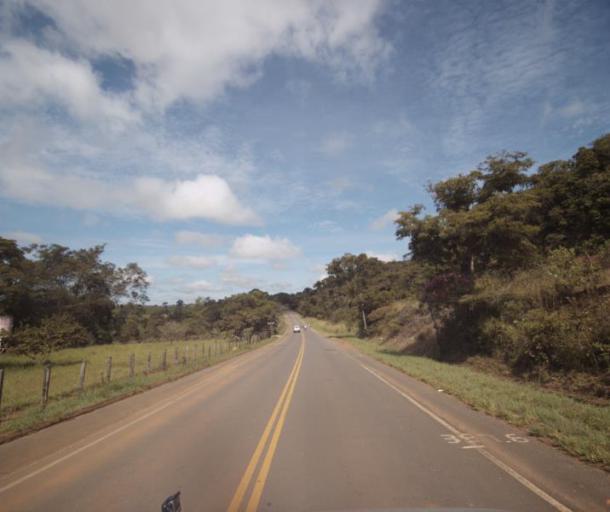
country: BR
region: Goias
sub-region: Pirenopolis
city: Pirenopolis
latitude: -15.9588
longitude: -48.8143
